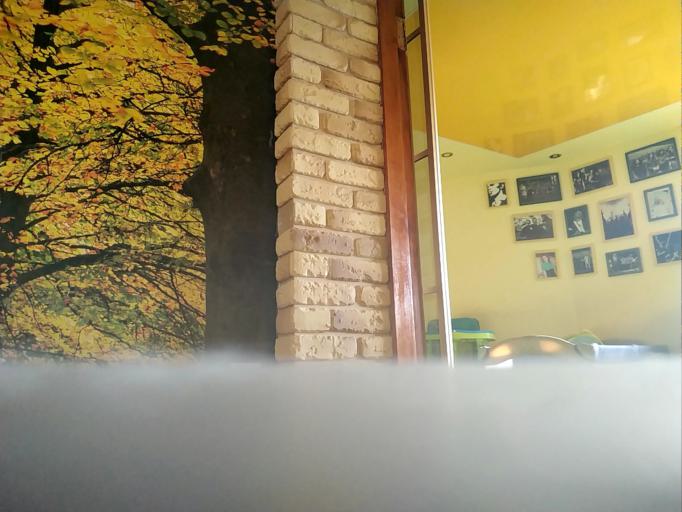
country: RU
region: Kaluga
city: Meshchovsk
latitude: 54.2387
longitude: 35.2268
